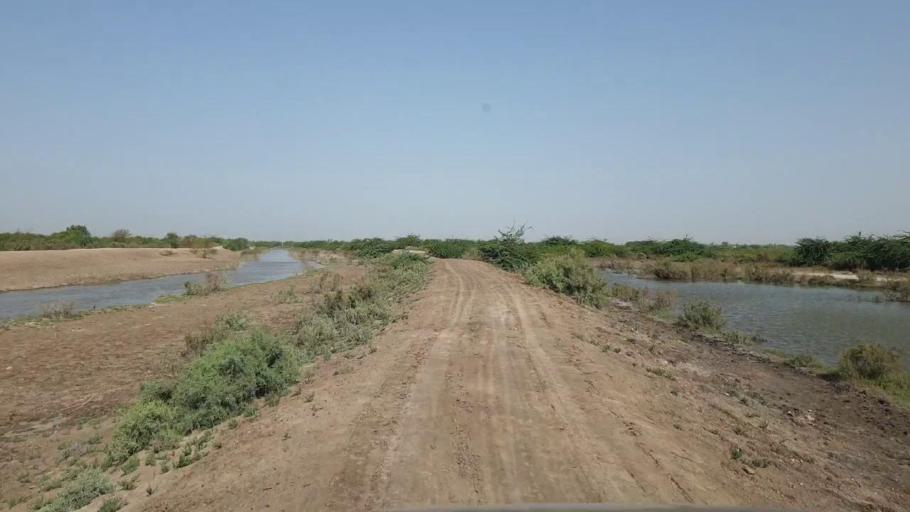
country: PK
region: Sindh
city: Tando Bago
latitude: 24.6566
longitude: 69.0702
